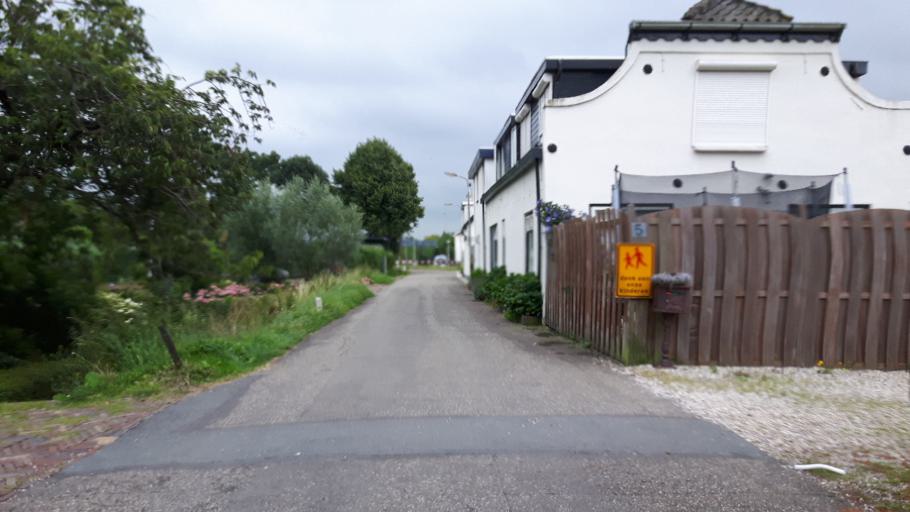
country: NL
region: South Holland
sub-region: Gemeente Alphen aan den Rijn
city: Alphen aan den Rijn
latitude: 52.1199
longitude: 4.6730
